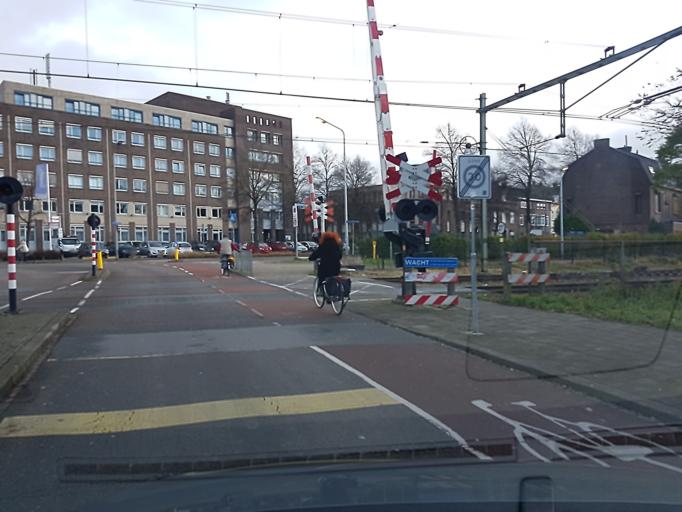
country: NL
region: Limburg
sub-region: Gemeente Maastricht
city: Maastricht
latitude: 50.8463
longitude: 5.7071
